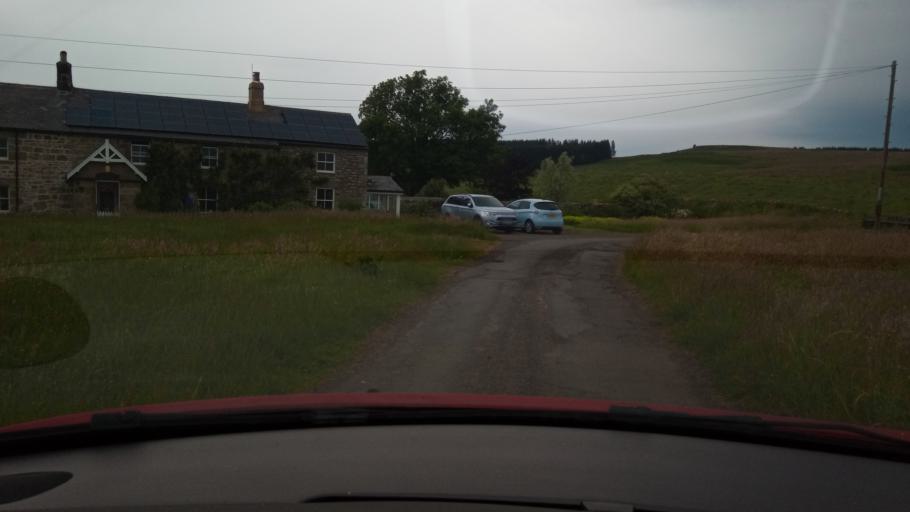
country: GB
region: England
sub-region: Northumberland
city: Rochester
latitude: 55.2814
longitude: -2.2644
